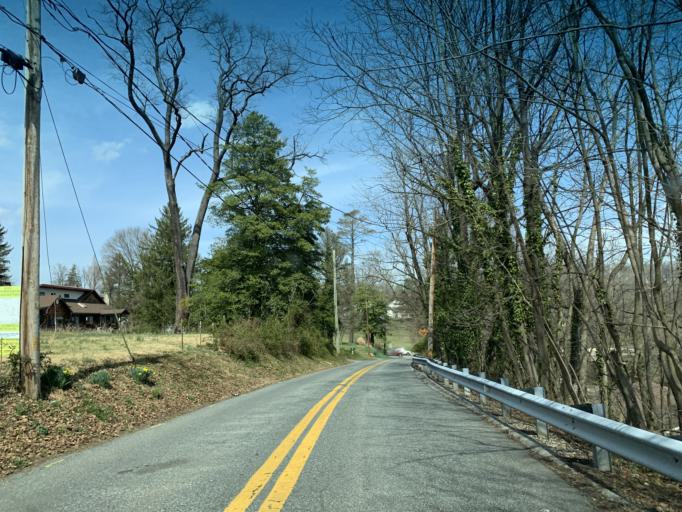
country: US
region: Delaware
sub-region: New Castle County
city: Newport
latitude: 39.7379
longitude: -75.6356
